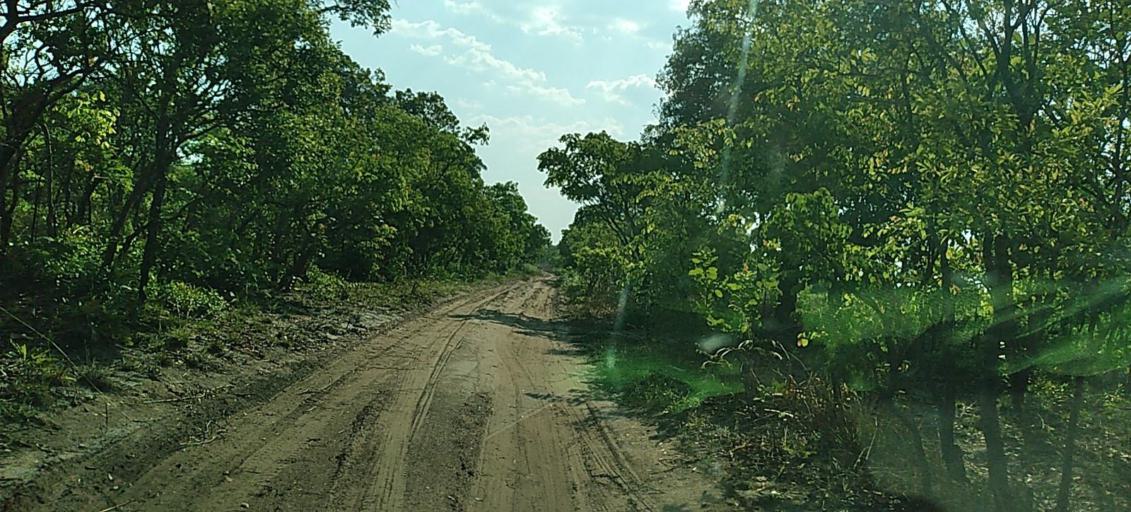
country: ZM
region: North-Western
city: Mwinilunga
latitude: -11.3083
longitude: 24.7867
